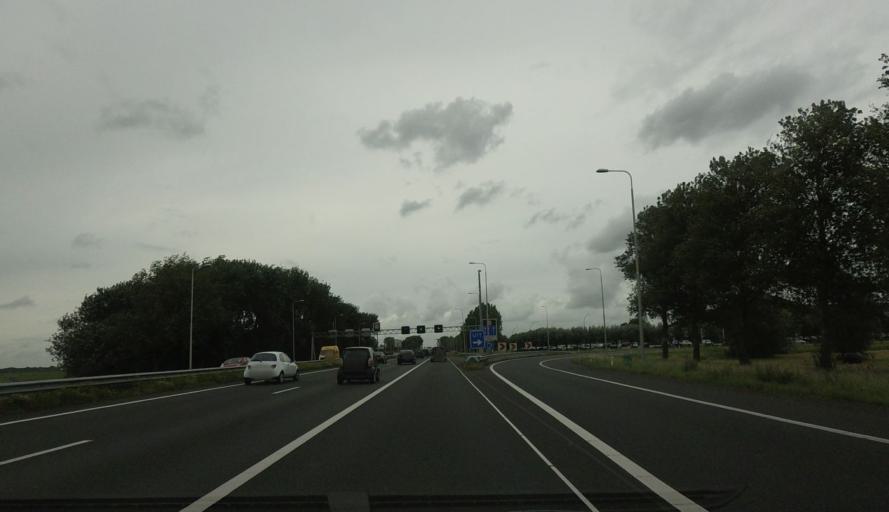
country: NL
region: North Holland
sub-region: Gemeente Uitgeest
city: Uitgeest
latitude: 52.5462
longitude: 4.7201
